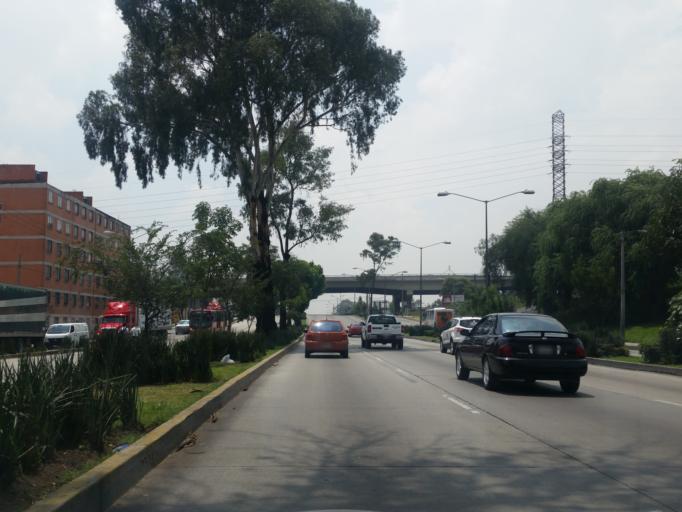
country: MX
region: Mexico City
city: Azcapotzalco
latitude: 19.5146
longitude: -99.1617
